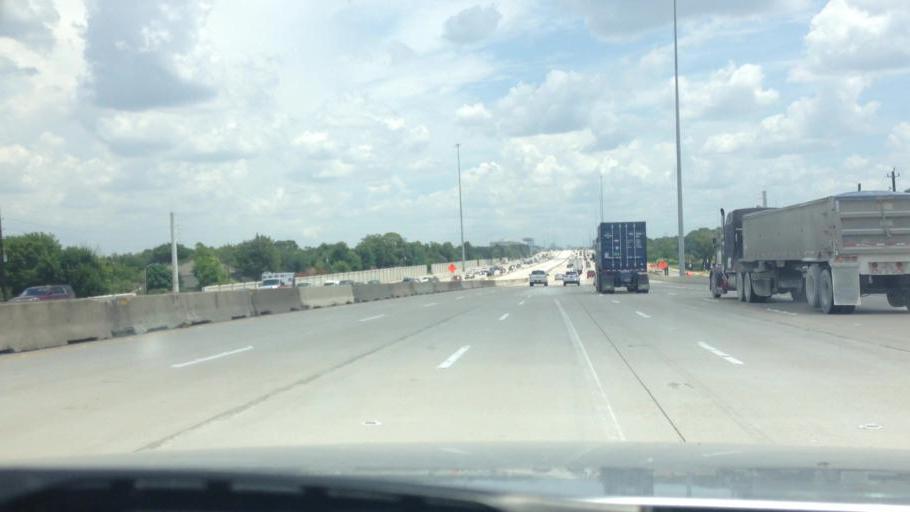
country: US
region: Texas
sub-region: Harris County
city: Spring Valley
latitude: 29.8304
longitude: -95.4815
